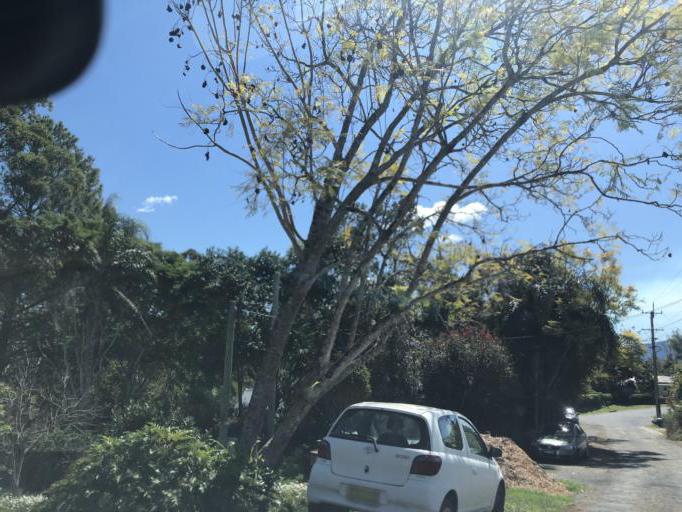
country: AU
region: New South Wales
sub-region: Bellingen
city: Bellingen
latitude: -30.4596
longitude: 152.8975
